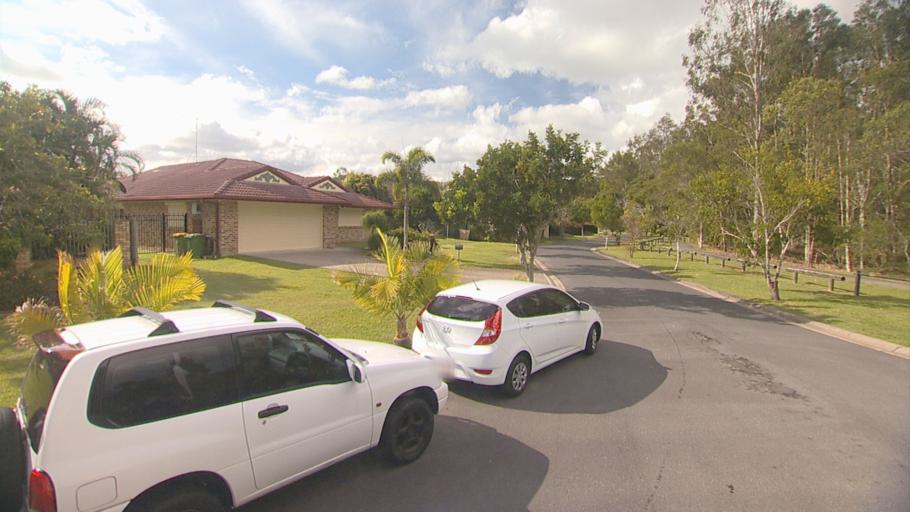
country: AU
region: Queensland
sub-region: Logan
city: Beenleigh
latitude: -27.6612
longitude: 153.2081
